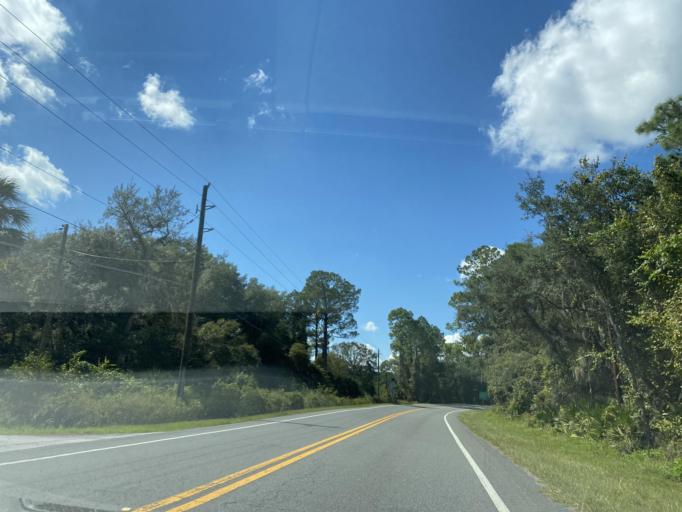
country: US
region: Florida
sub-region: Lake County
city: Lake Mack-Forest Hills
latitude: 29.0146
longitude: -81.4639
